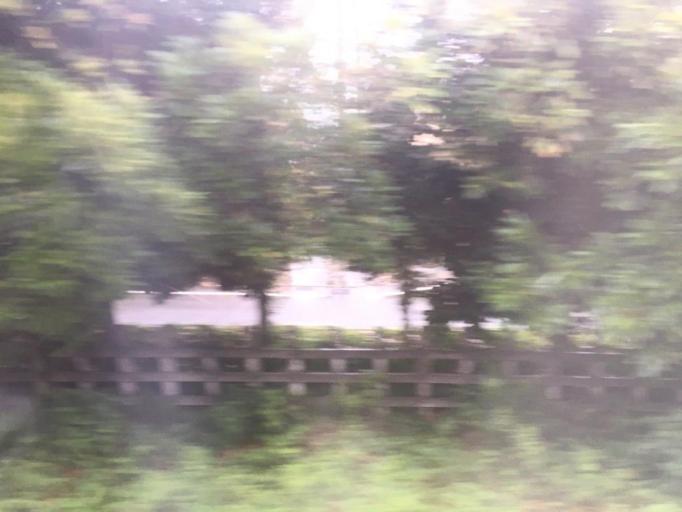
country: JP
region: Gunma
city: Ota
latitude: 36.3029
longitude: 139.3955
